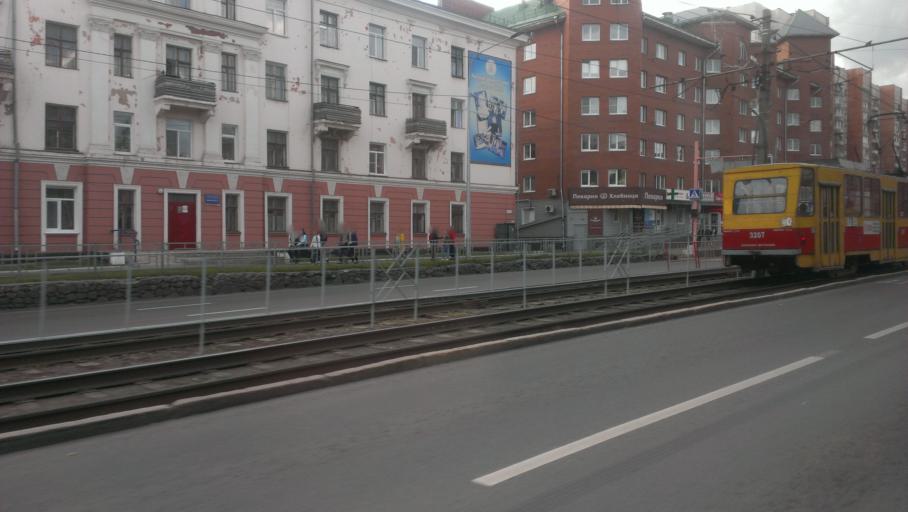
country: RU
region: Altai Krai
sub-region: Gorod Barnaulskiy
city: Barnaul
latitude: 53.3422
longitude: 83.7696
